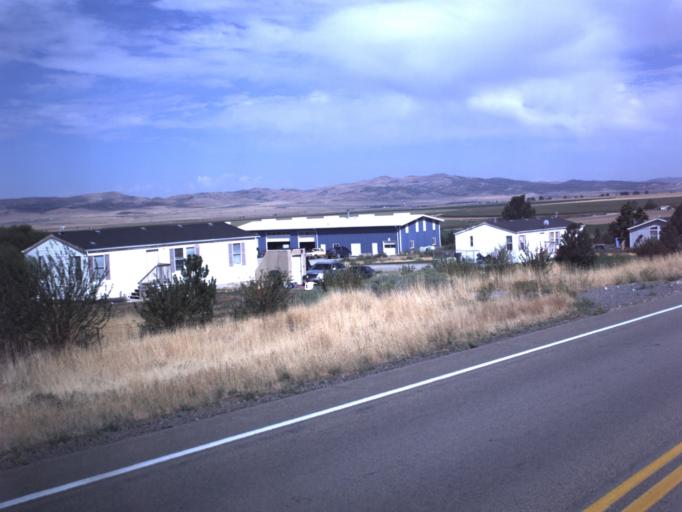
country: US
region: Utah
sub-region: Juab County
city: Nephi
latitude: 39.5203
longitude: -111.8679
